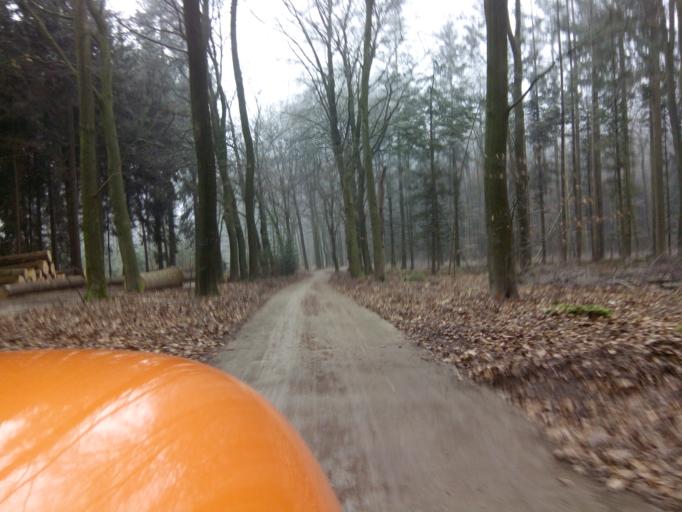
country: NL
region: Gelderland
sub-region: Gemeente Putten
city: Putten
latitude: 52.2566
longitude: 5.6576
